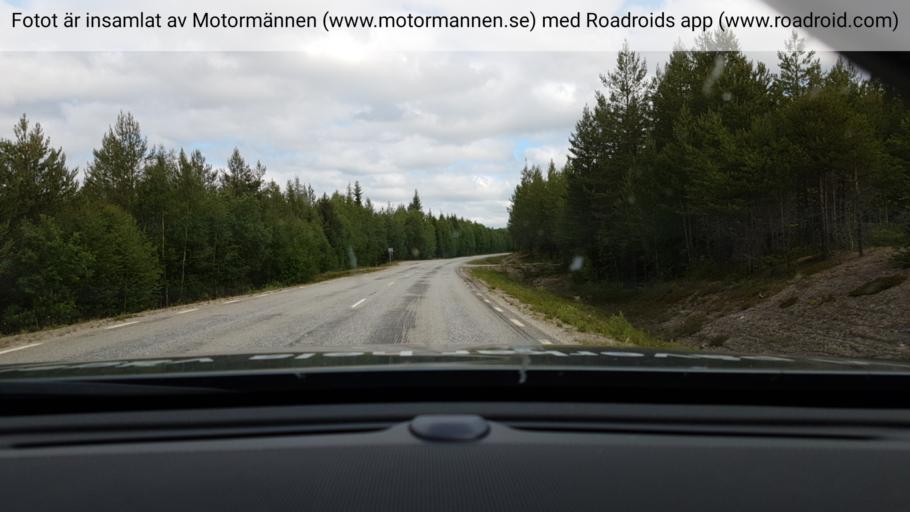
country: SE
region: Vaesterbotten
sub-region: Mala Kommun
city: Mala
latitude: 64.9268
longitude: 18.6181
